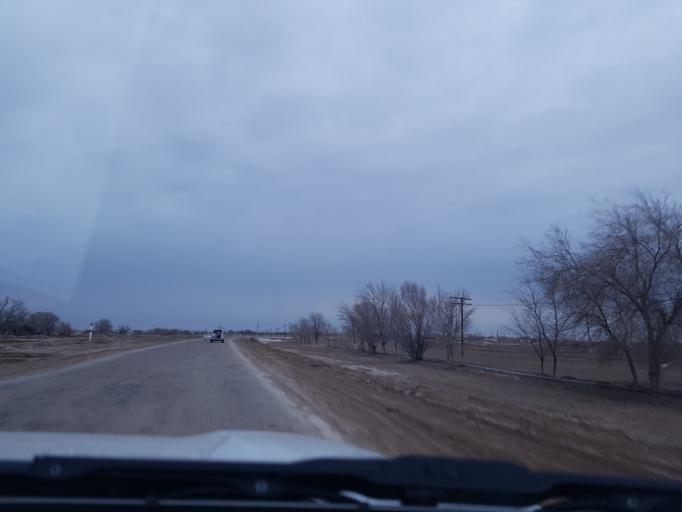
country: TM
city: Akdepe
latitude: 41.9653
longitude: 59.4976
